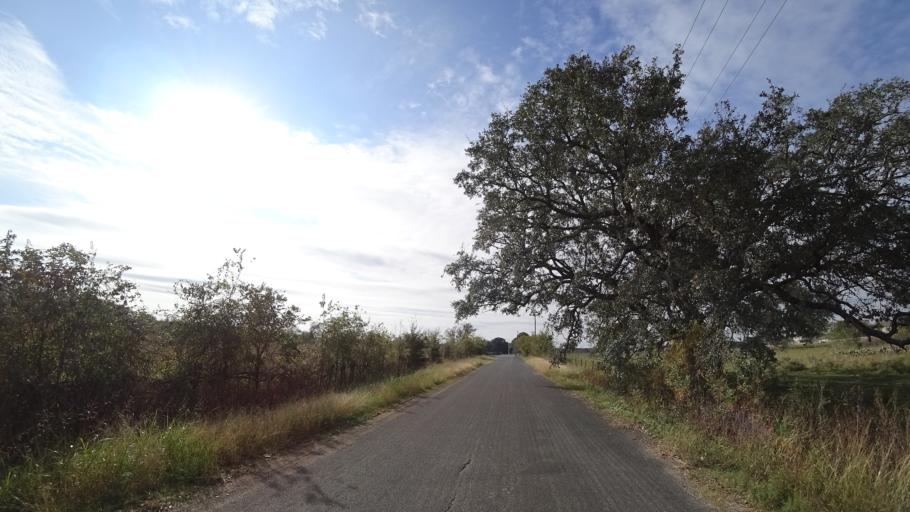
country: US
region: Texas
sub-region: Travis County
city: Manchaca
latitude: 30.1342
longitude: -97.8456
